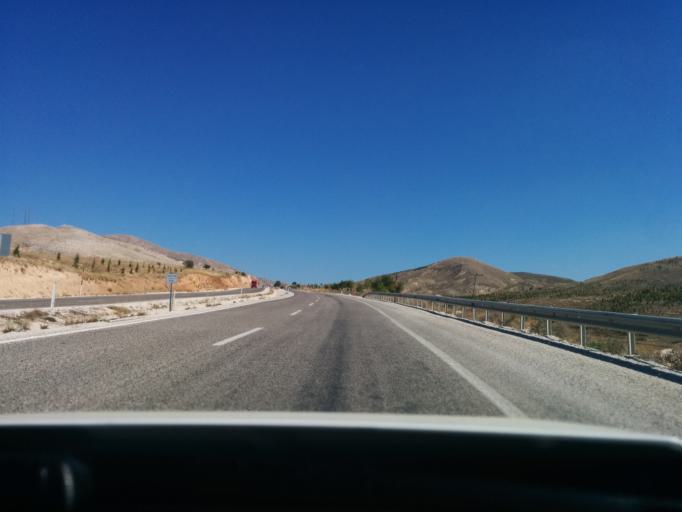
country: TR
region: Antalya
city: Kizilcadag
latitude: 37.0161
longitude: 29.9689
